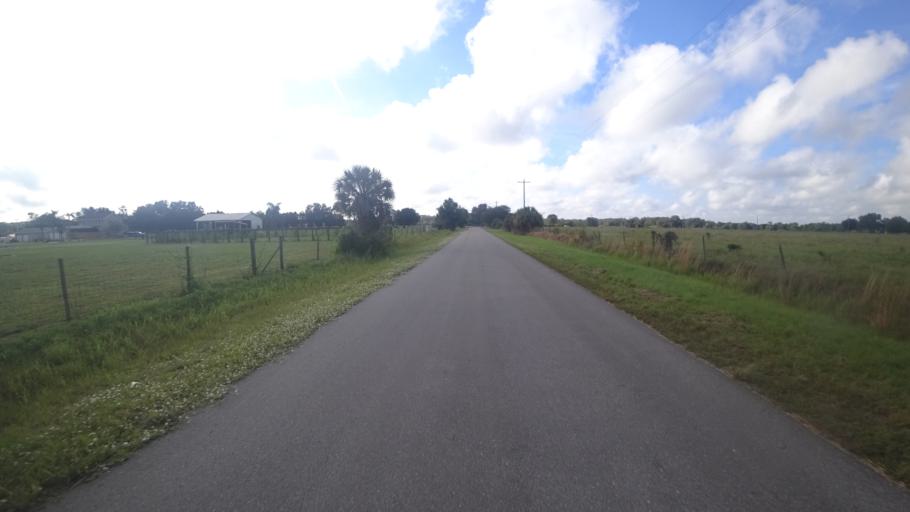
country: US
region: Florida
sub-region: Hillsborough County
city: Sun City Center
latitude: 27.5941
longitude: -82.3863
